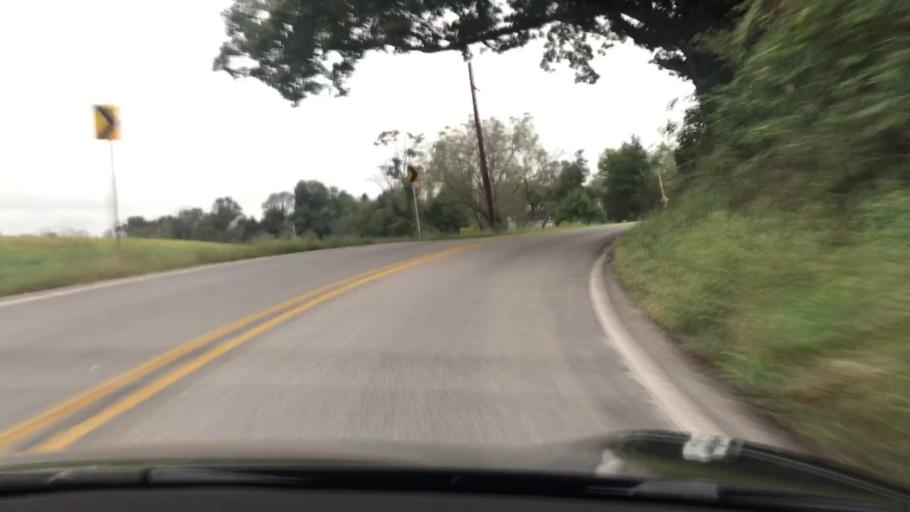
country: US
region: Pennsylvania
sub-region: York County
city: Weigelstown
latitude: 39.9482
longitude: -76.8622
